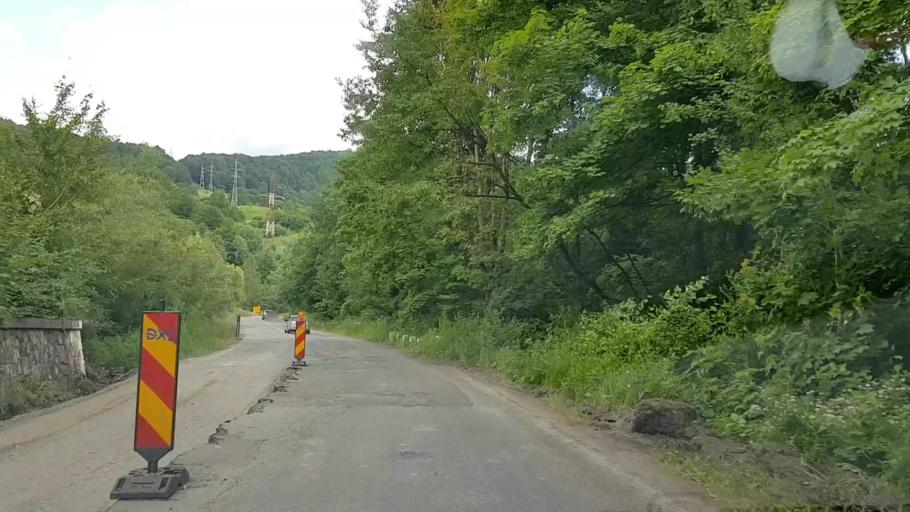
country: RO
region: Neamt
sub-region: Comuna Pangarati
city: Pangarati
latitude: 46.9409
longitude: 26.1251
